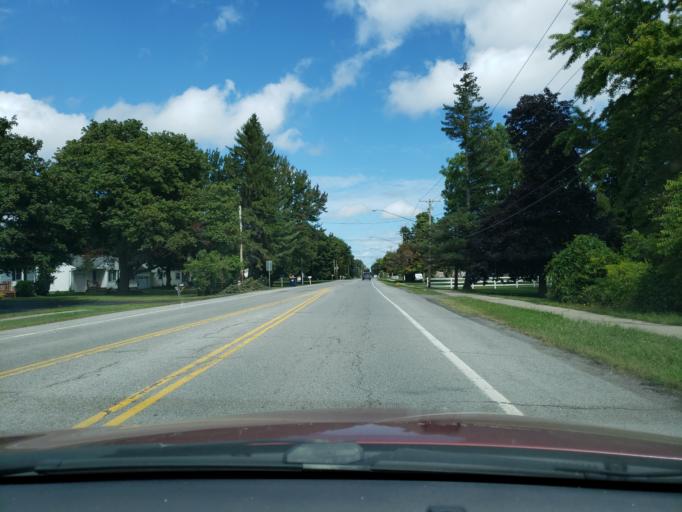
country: US
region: New York
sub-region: Monroe County
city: Greece
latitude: 43.2288
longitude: -77.7336
